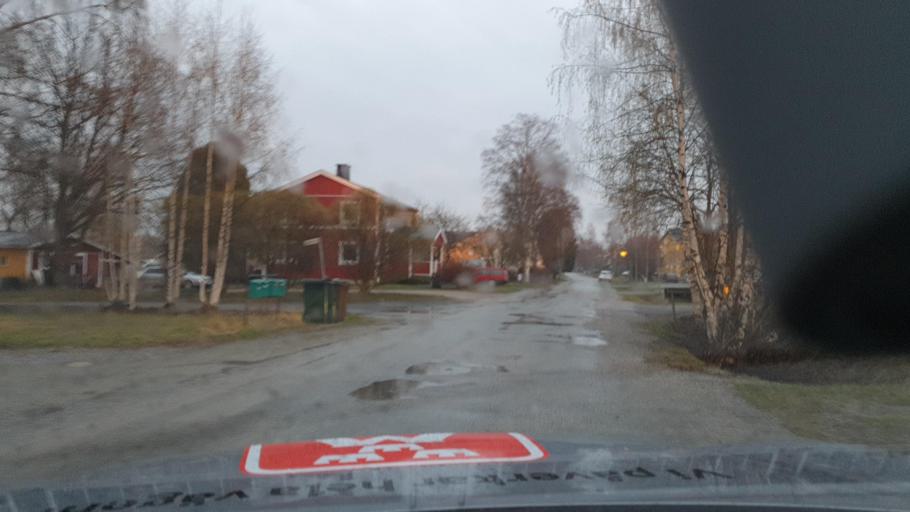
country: SE
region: Vaesternorrland
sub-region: OErnskoeldsviks Kommun
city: Ornskoldsvik
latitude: 63.2732
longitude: 18.6626
